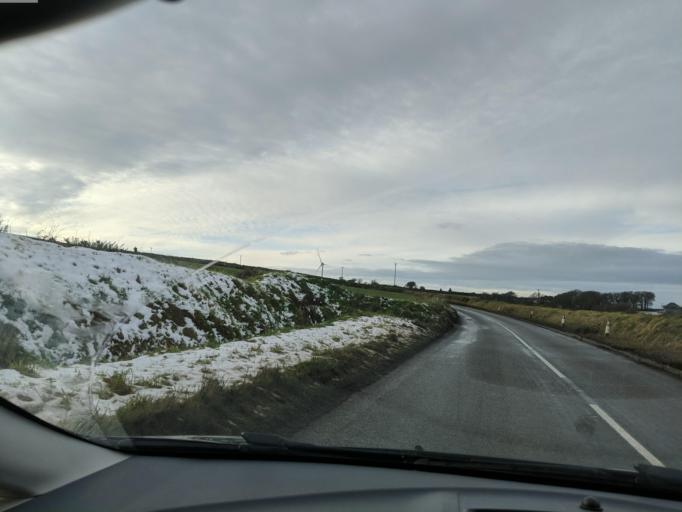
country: GB
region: England
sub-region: Cornwall
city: Jacobstow
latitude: 50.6641
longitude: -4.5848
